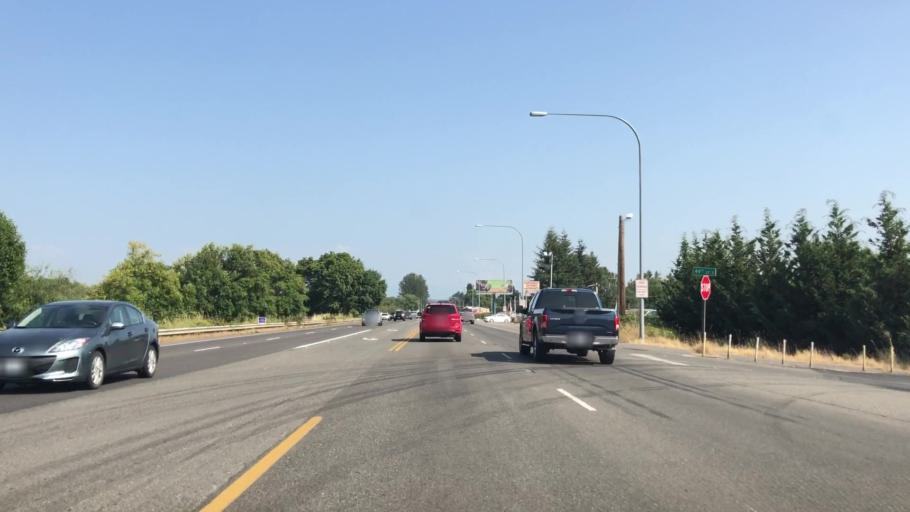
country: US
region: Washington
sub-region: Pierce County
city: Fife
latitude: 47.2174
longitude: -122.3487
